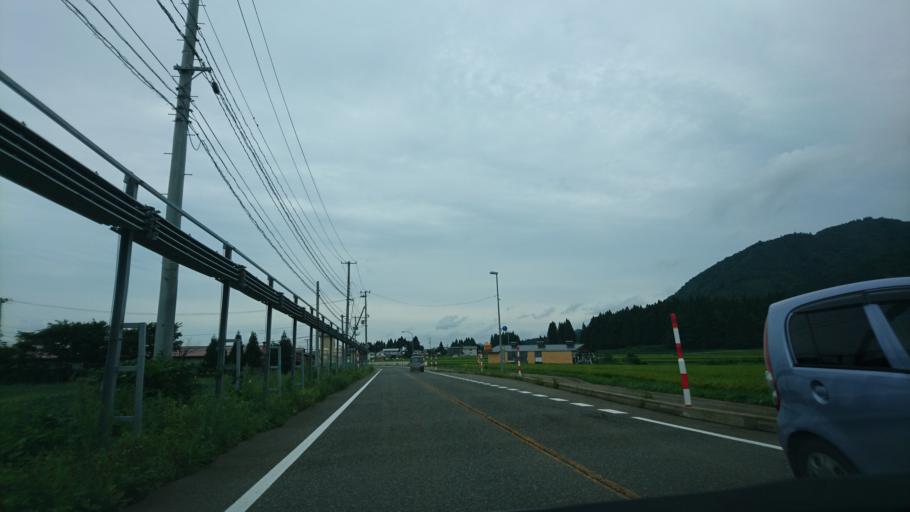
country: JP
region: Akita
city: Yuzawa
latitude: 39.1220
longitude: 140.5780
